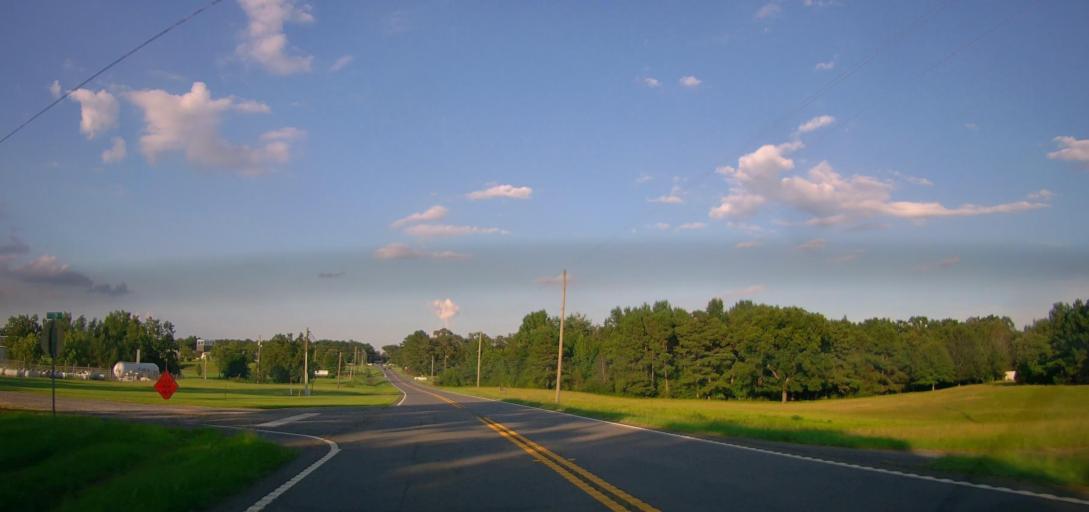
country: US
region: Georgia
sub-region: Crawford County
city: Roberta
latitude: 32.7114
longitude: -84.0239
